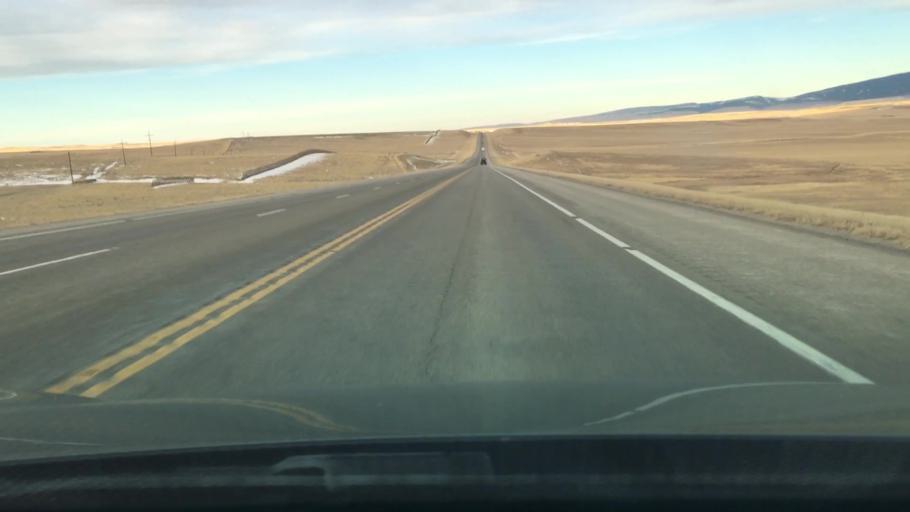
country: US
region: Montana
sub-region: Wheatland County
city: Harlowton
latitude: 46.6357
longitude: -109.7634
